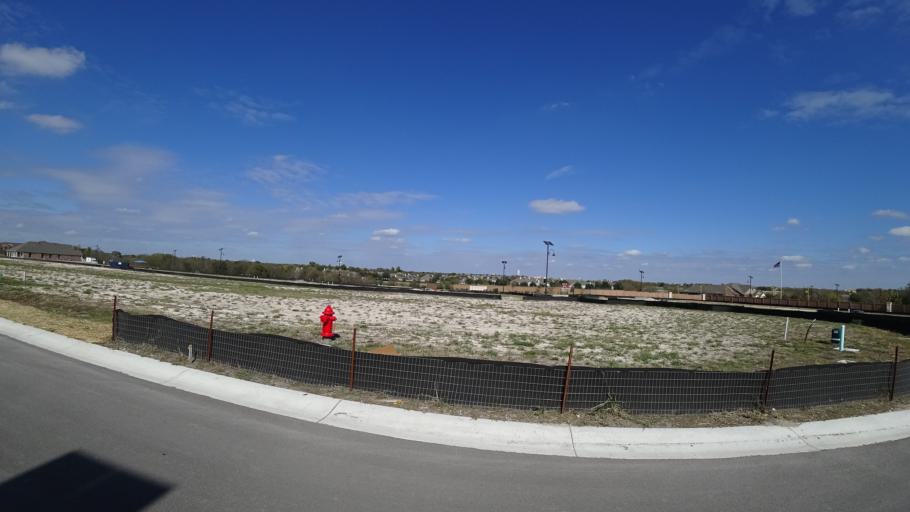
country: US
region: Texas
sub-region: Travis County
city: Pflugerville
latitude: 30.4510
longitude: -97.6311
